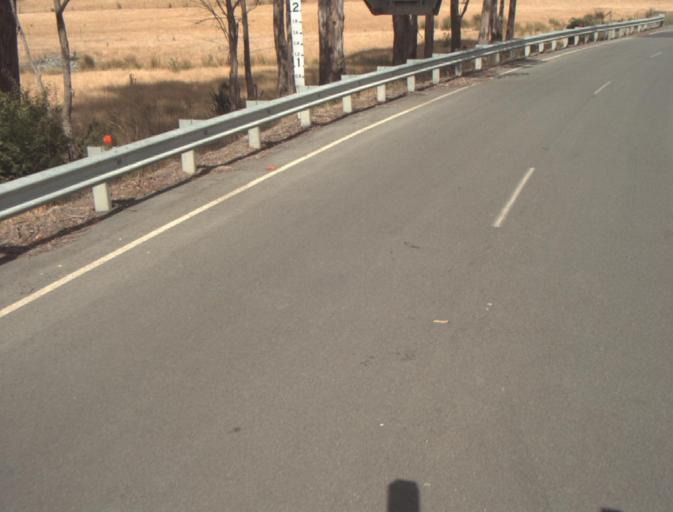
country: AU
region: Tasmania
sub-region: Launceston
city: Mayfield
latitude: -41.2093
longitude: 147.1262
